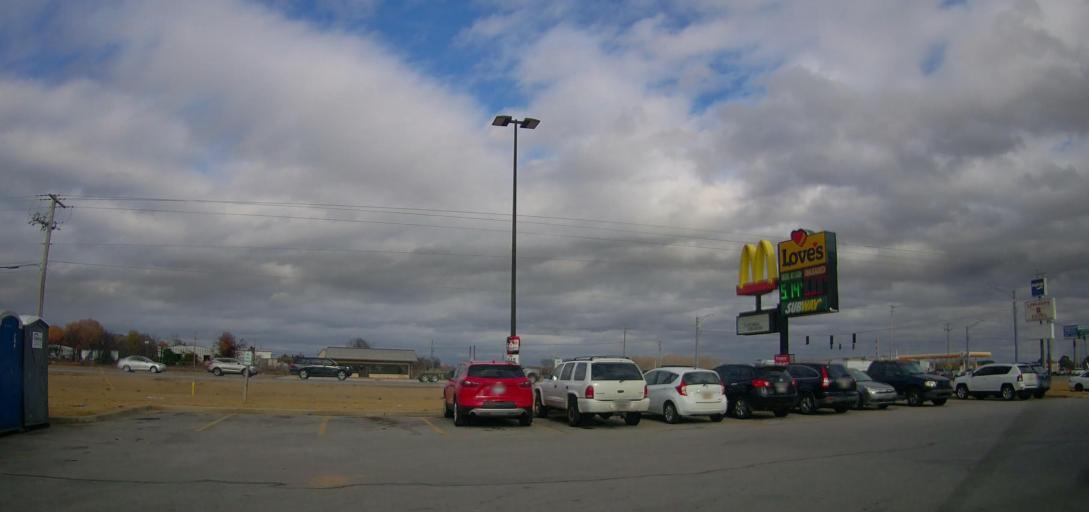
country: US
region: Alabama
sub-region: Colbert County
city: Muscle Shoals
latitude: 34.6976
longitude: -87.6359
